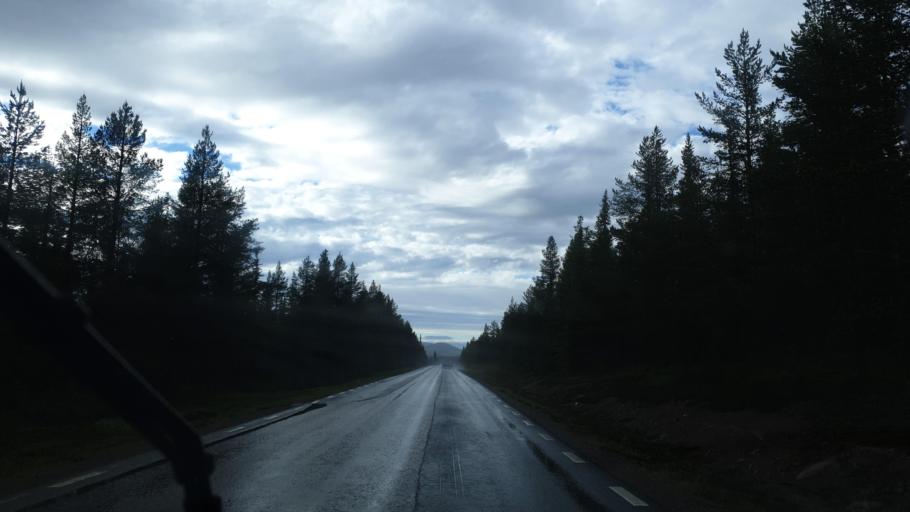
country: SE
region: Norrbotten
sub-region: Arjeplogs Kommun
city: Arjeplog
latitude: 65.8110
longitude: 18.4547
